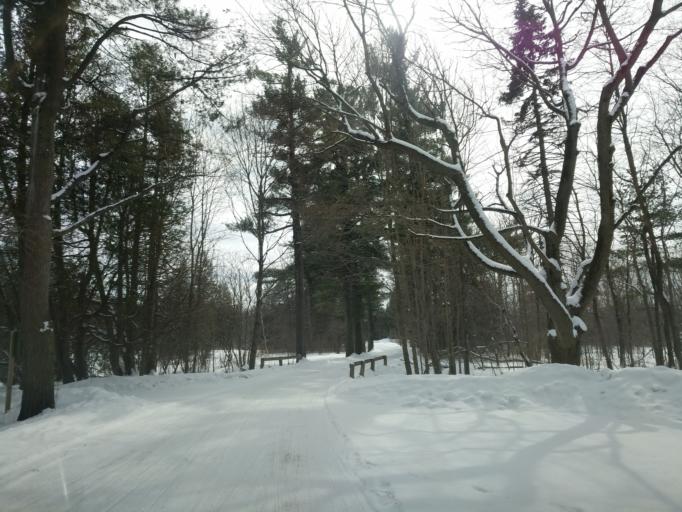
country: CA
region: Ontario
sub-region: York
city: Richmond Hill
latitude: 43.9541
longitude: -79.4233
